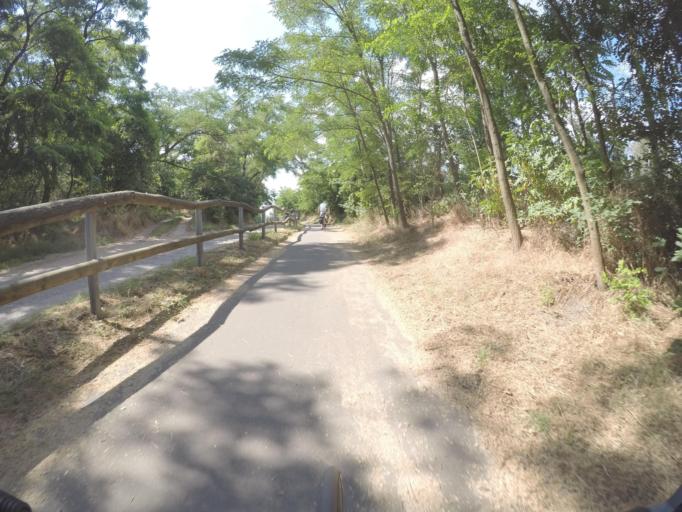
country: DE
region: Brandenburg
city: Ketzin
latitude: 52.4639
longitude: 12.8099
